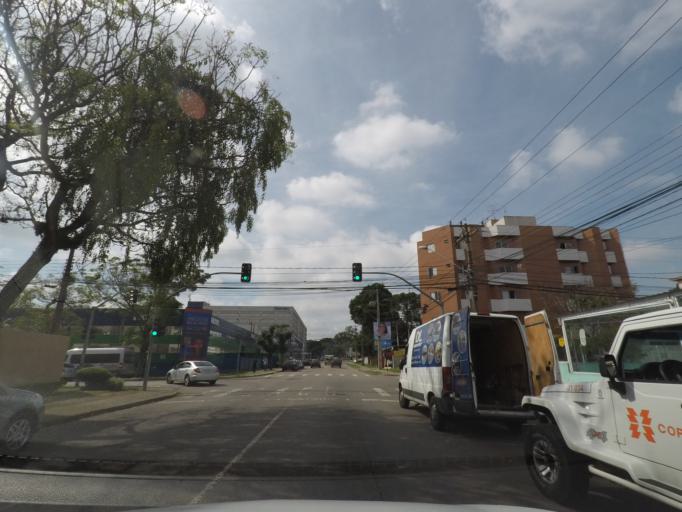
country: BR
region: Parana
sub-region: Curitiba
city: Curitiba
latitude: -25.4794
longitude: -49.2972
